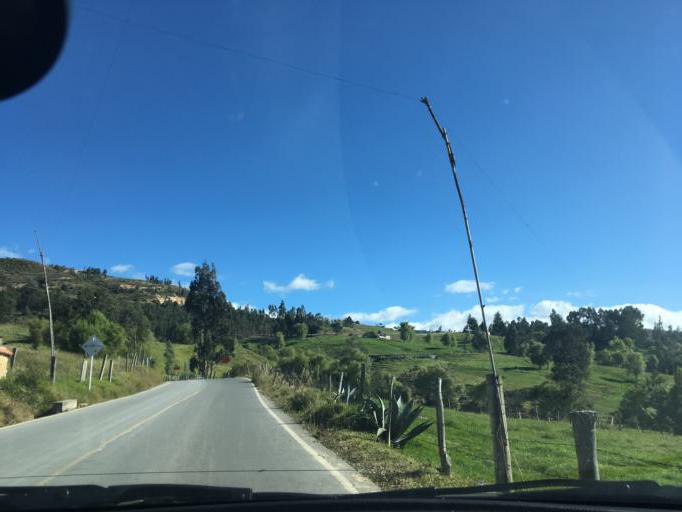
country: CO
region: Boyaca
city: Firavitoba
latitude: 5.5992
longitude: -72.9796
